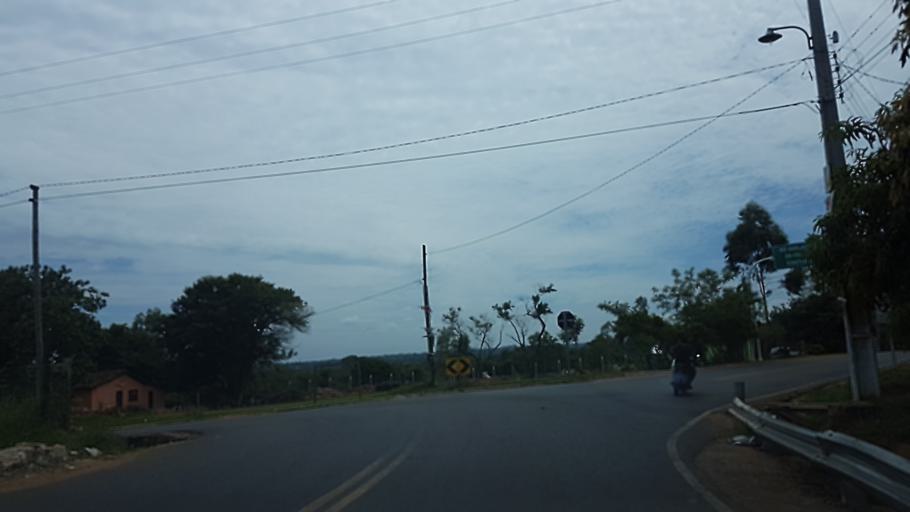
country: PY
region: Central
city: Capiata
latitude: -25.3182
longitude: -57.4531
